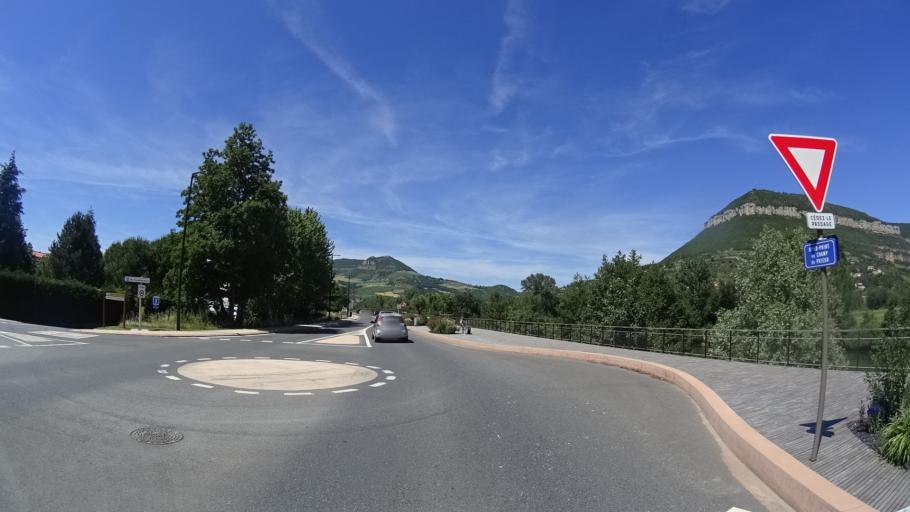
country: FR
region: Midi-Pyrenees
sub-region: Departement de l'Aveyron
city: Millau
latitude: 44.0982
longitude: 3.0875
